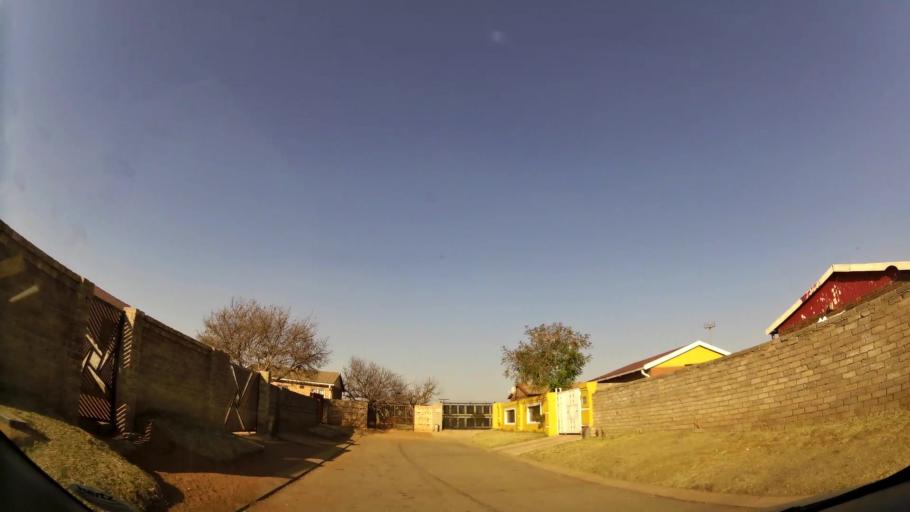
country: ZA
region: Gauteng
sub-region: West Rand District Municipality
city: Randfontein
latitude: -26.1996
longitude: 27.7032
